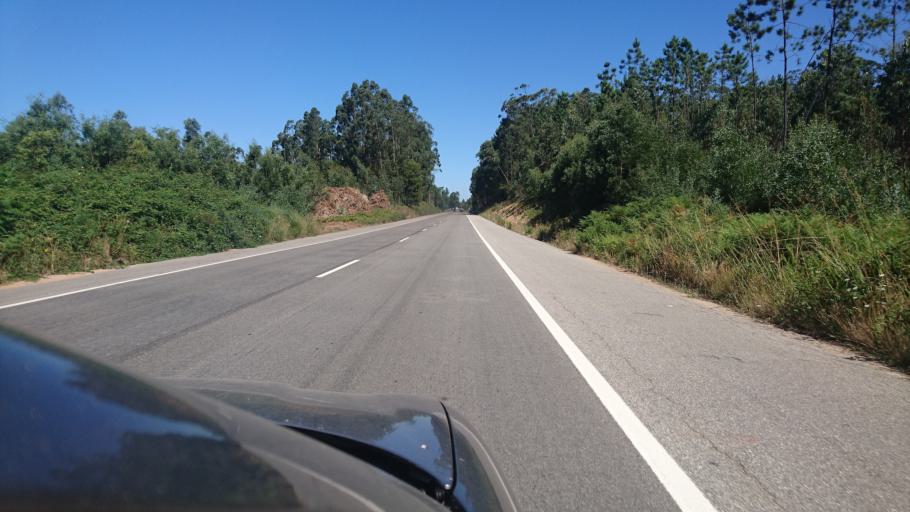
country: PT
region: Aveiro
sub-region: Santa Maria da Feira
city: Rio Meao
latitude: 40.9425
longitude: -8.5838
